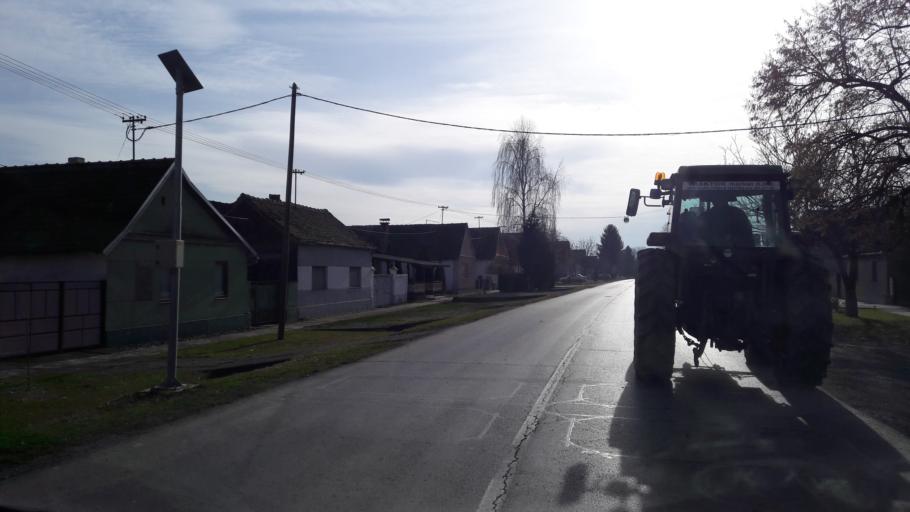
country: HR
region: Osjecko-Baranjska
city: Semeljci
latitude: 45.3048
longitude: 18.5595
